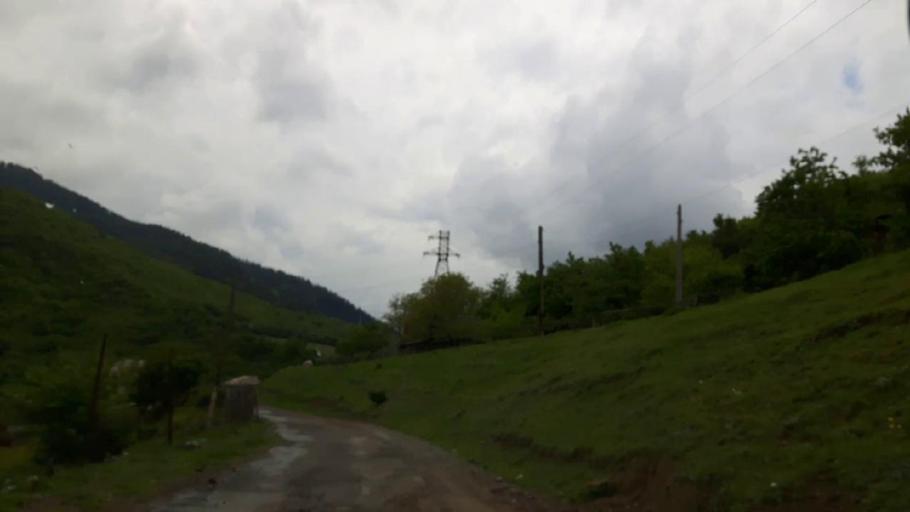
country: GE
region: Shida Kartli
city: Gori
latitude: 41.8902
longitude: 44.0093
